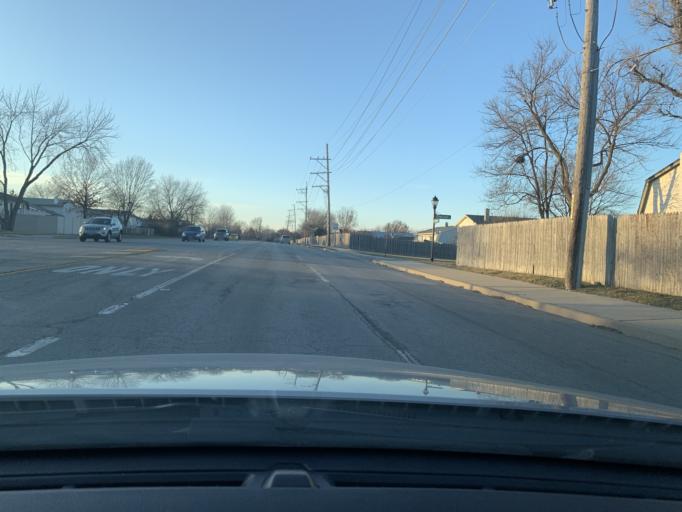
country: US
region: Illinois
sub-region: DuPage County
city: Itasca
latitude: 41.9966
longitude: -88.0324
